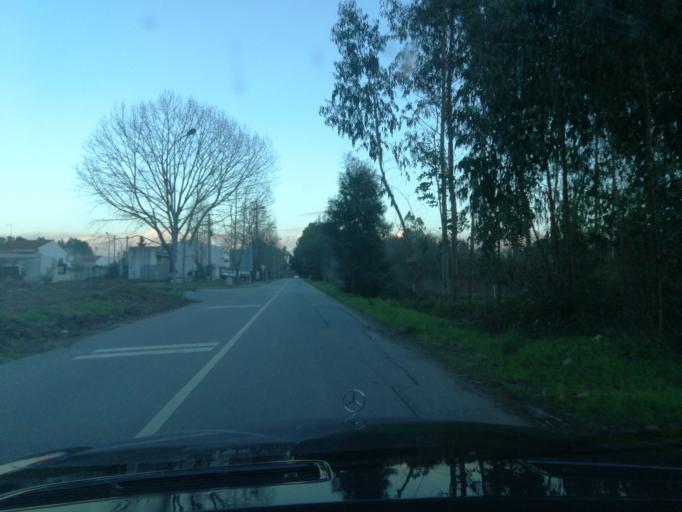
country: PT
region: Aveiro
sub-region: Estarreja
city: Estarreja
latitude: 40.7578
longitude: -8.5941
